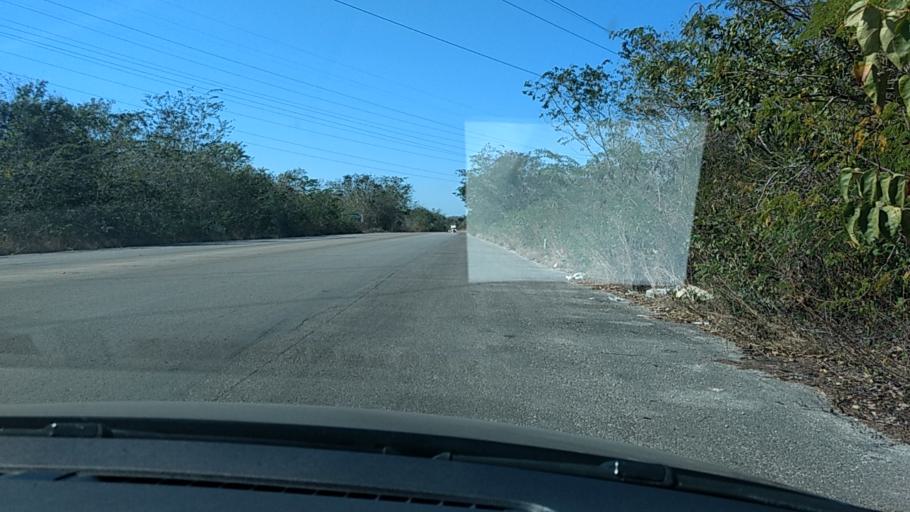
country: MX
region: Yucatan
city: Valladolid
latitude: 20.7018
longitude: -88.2418
